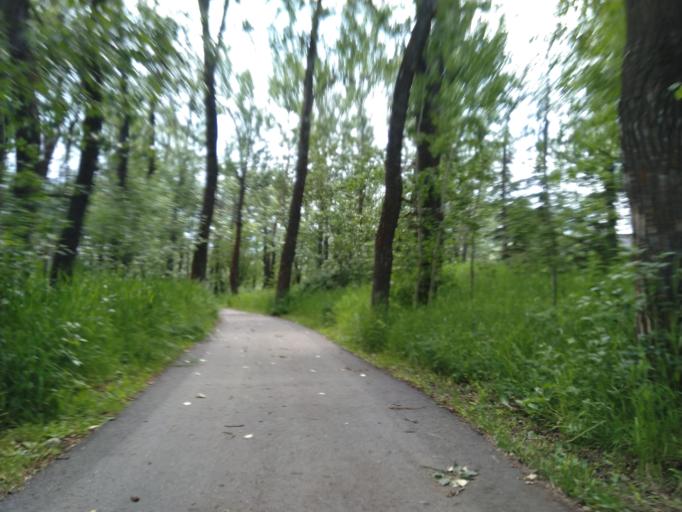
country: CA
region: Alberta
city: Cochrane
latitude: 51.1878
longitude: -114.4956
